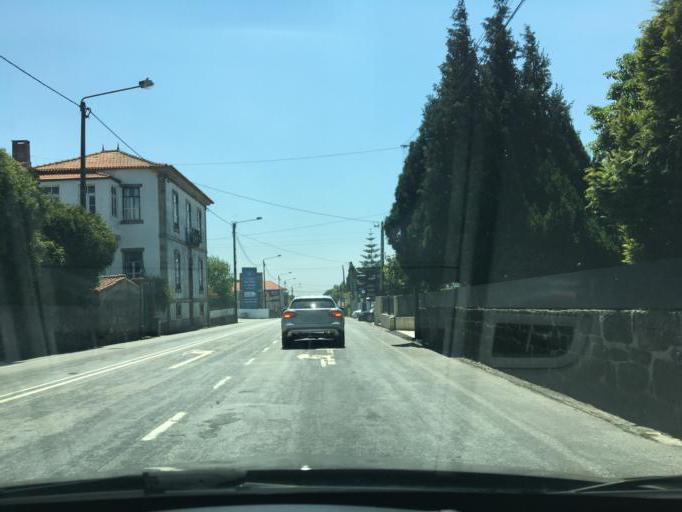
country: PT
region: Porto
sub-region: Maia
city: Gemunde
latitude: 41.2479
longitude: -8.6490
